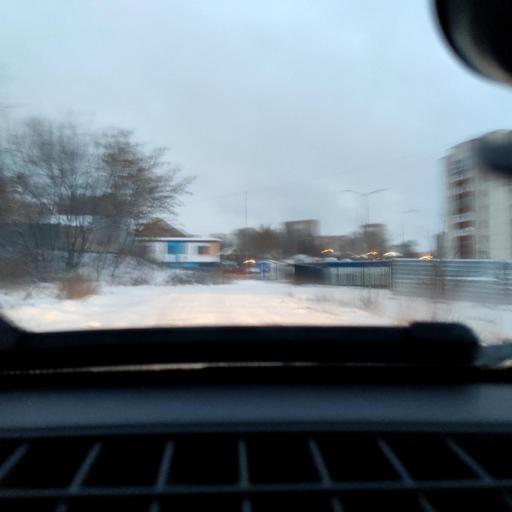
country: RU
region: Bashkortostan
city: Ufa
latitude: 54.7803
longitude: 56.0460
